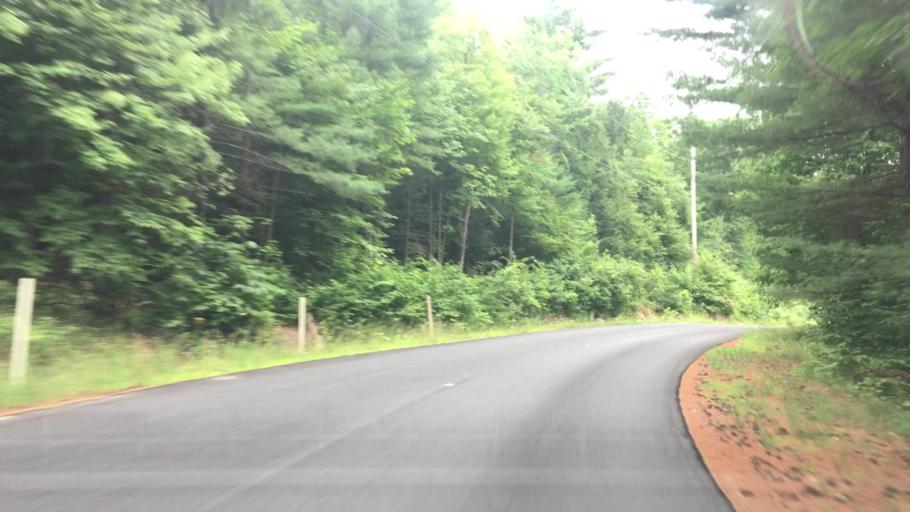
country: US
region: New York
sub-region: Essex County
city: Keeseville
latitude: 44.4191
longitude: -73.6359
